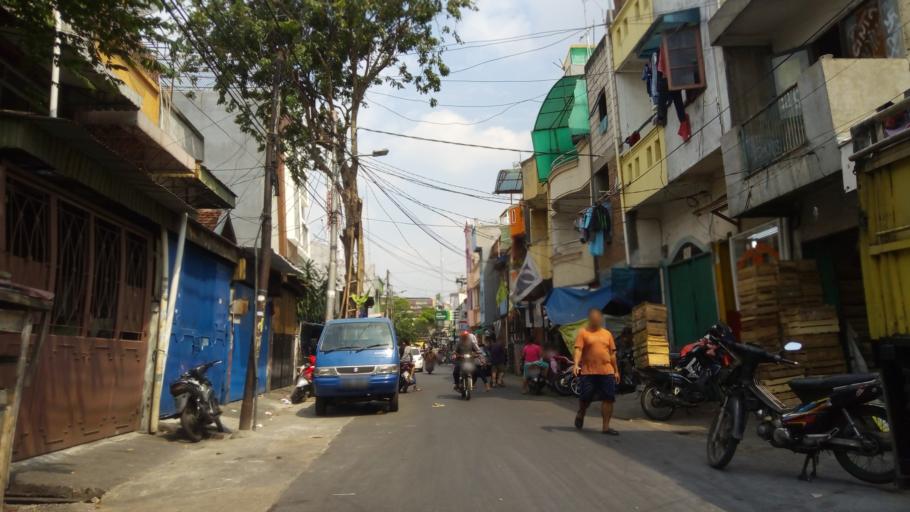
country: ID
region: Jakarta Raya
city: Jakarta
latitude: -6.1567
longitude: 106.8292
